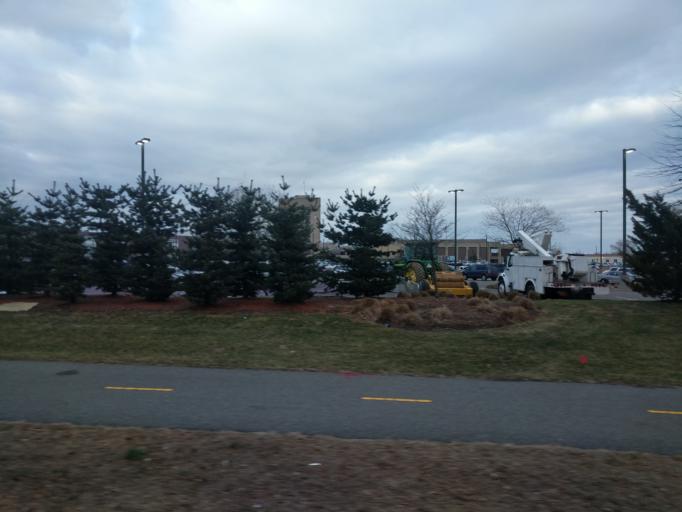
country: US
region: New York
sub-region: Nassau County
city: East Garden City
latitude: 40.7262
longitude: -73.5938
